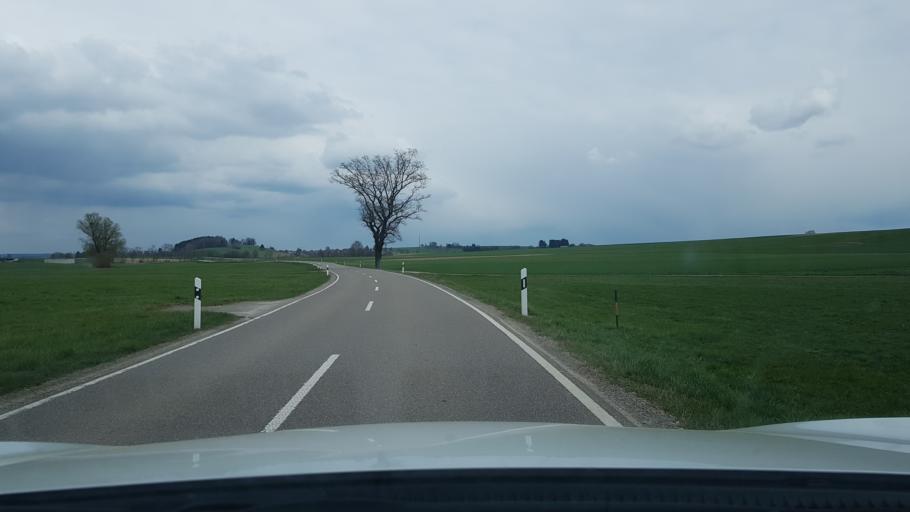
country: DE
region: Baden-Wuerttemberg
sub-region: Tuebingen Region
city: Warthausen
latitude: 48.1815
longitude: 9.7651
